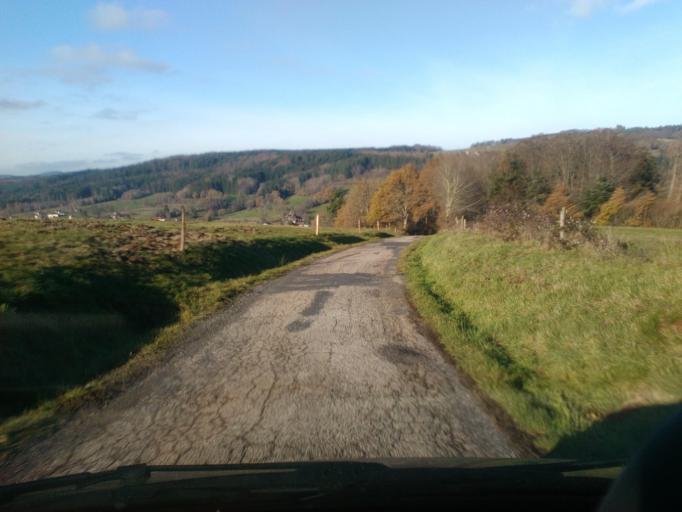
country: FR
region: Lorraine
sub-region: Departement des Vosges
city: Saint-Die-des-Vosges
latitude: 48.3370
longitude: 6.9669
